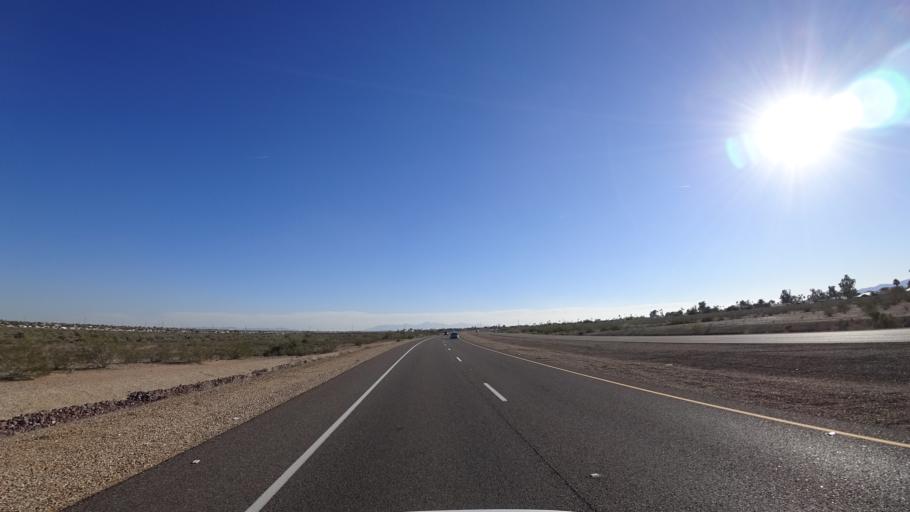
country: US
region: Arizona
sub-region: Maricopa County
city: Sun City West
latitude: 33.6513
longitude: -112.3224
